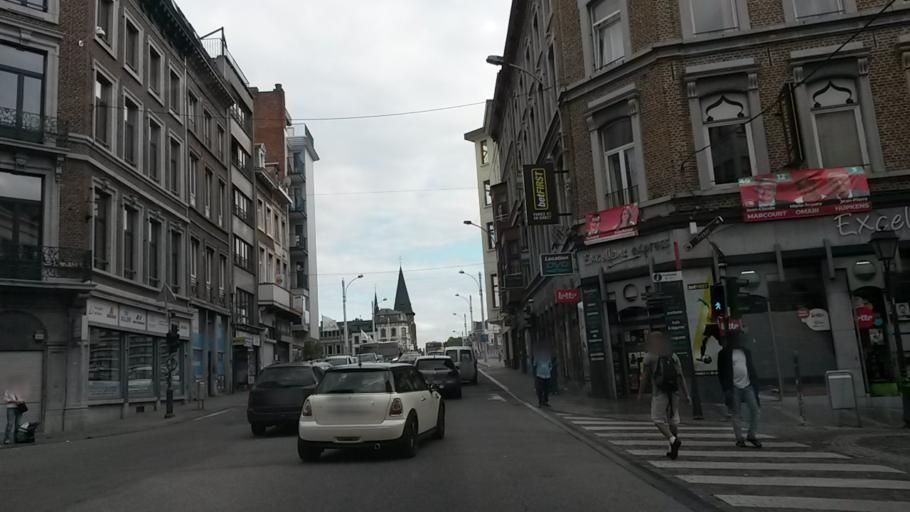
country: BE
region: Wallonia
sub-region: Province de Liege
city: Liege
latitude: 50.6441
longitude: 5.5771
